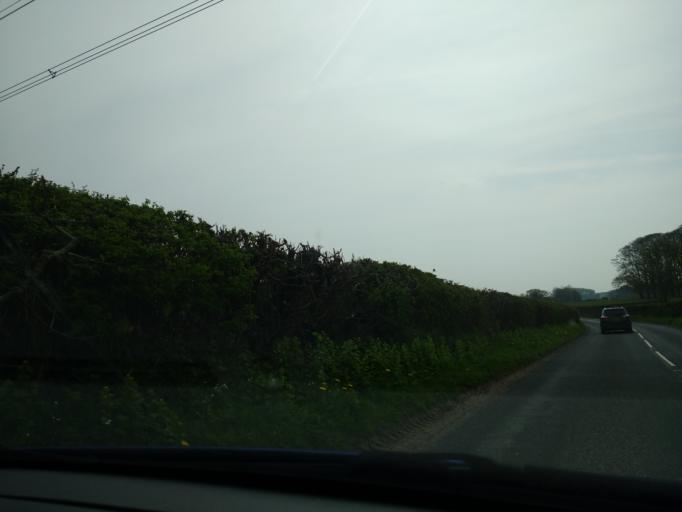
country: GB
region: England
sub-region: Lancashire
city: Lancaster
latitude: 54.0165
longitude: -2.8119
